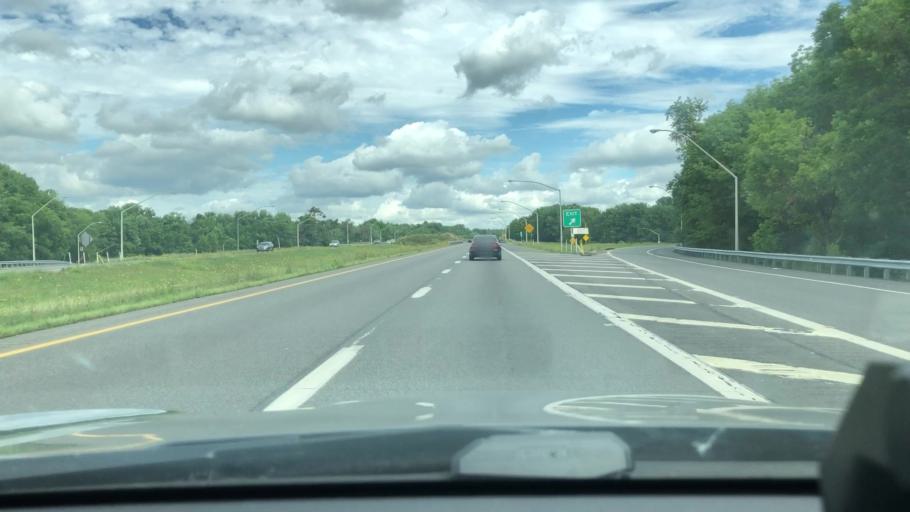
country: US
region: Pennsylvania
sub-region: Northampton County
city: Belfast
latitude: 40.7764
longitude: -75.2810
